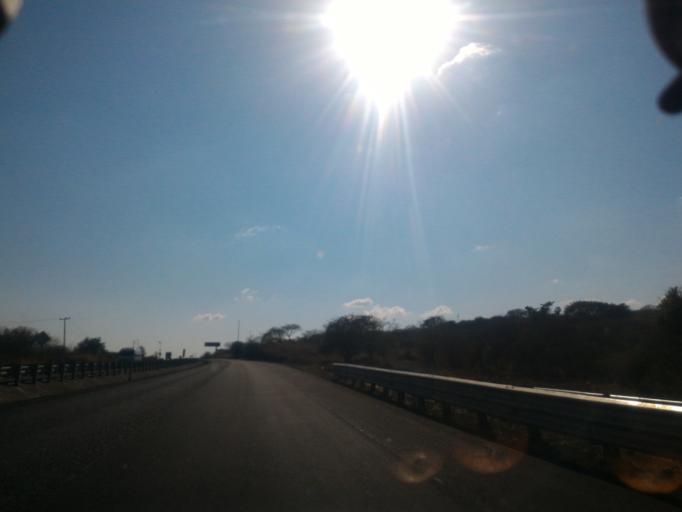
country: MX
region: Jalisco
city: Tonila
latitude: 19.4199
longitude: -103.5178
